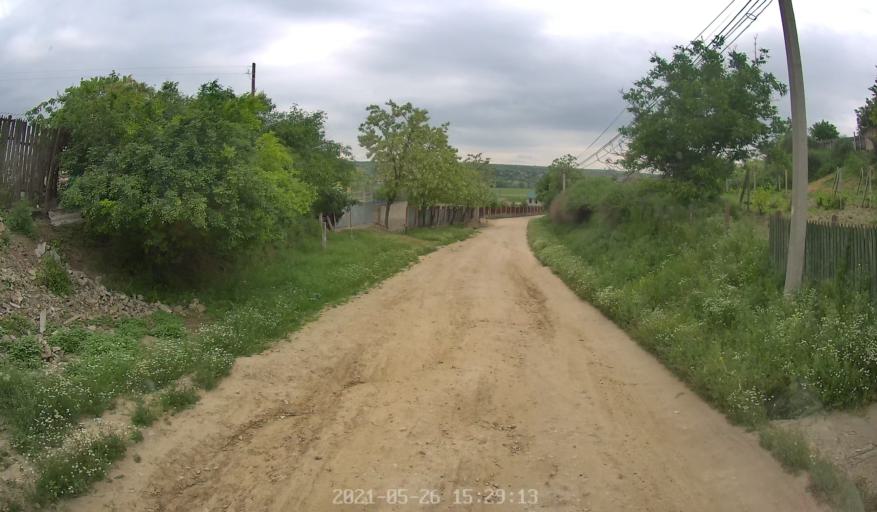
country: MD
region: Hincesti
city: Dancu
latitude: 46.6677
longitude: 28.3210
